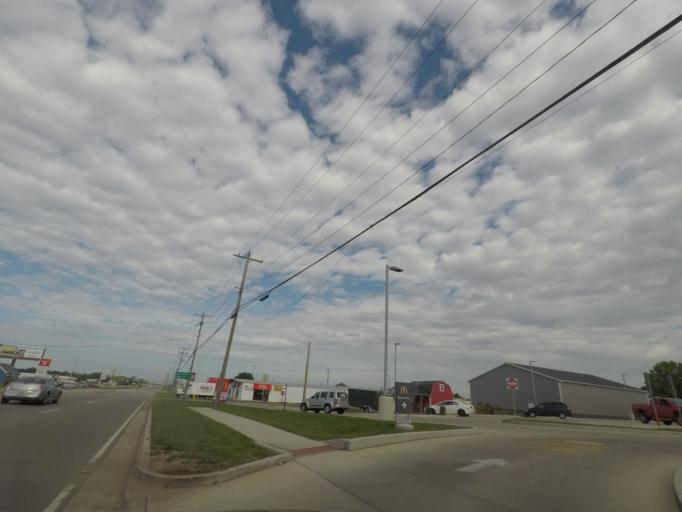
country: US
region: Illinois
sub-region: Logan County
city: Lincoln
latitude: 40.1578
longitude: -89.3877
